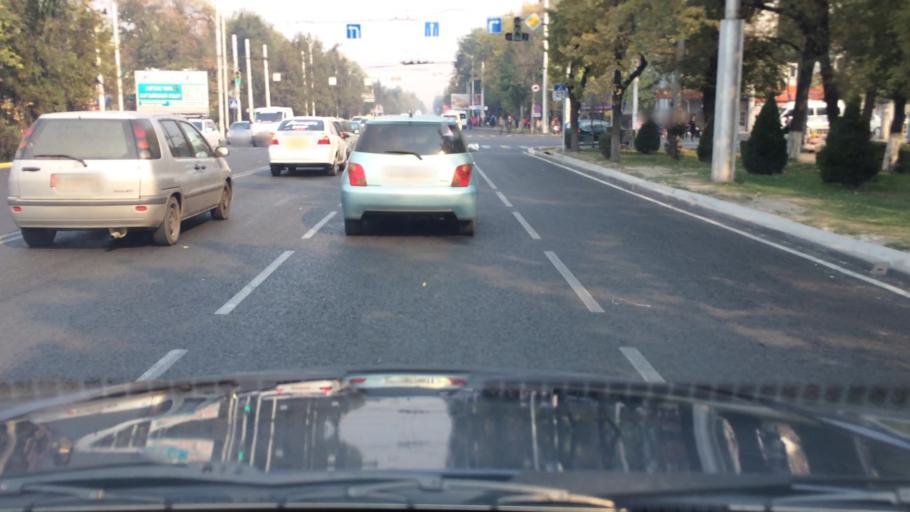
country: KG
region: Chuy
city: Bishkek
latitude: 42.8431
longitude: 74.5861
